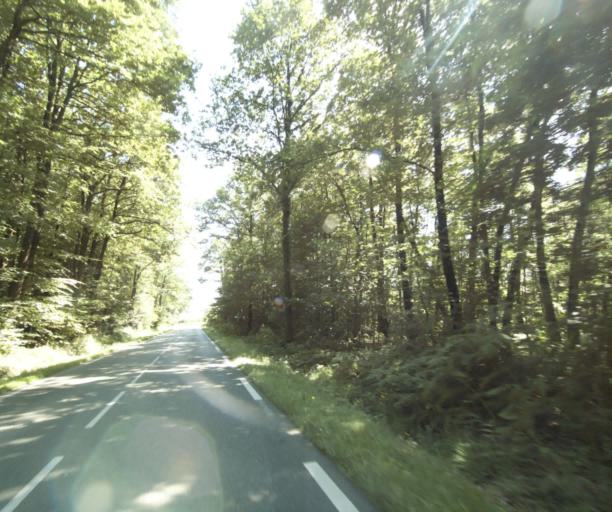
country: FR
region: Pays de la Loire
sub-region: Departement de la Mayenne
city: Laval
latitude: 48.0357
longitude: -0.7771
